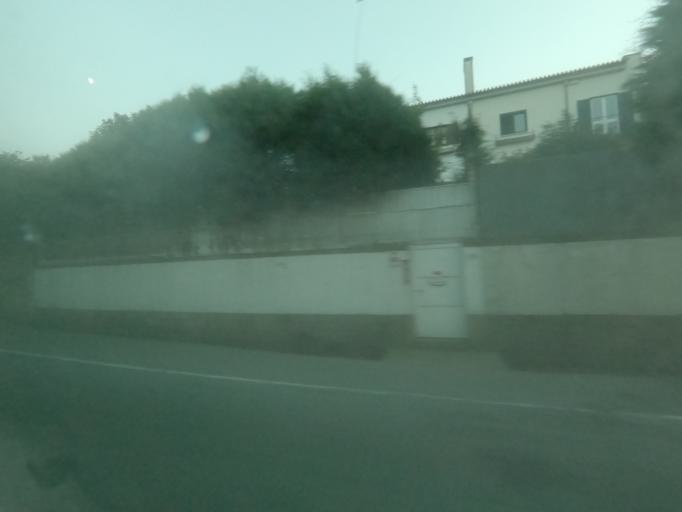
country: PT
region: Porto
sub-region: Matosinhos
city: Sao Mamede de Infesta
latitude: 41.1827
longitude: -8.6173
